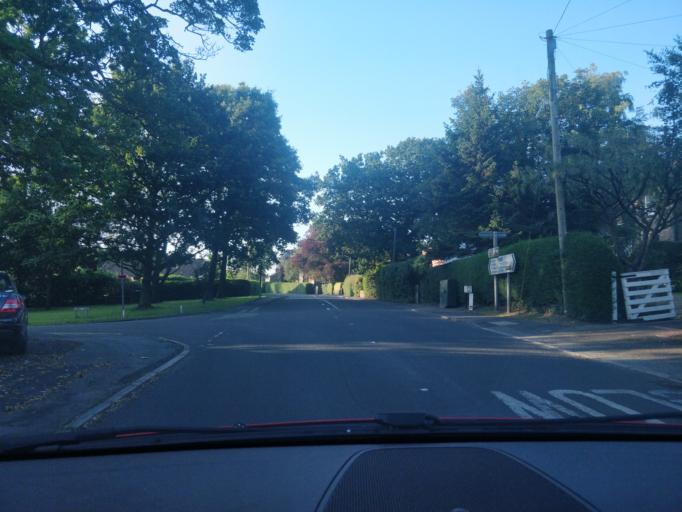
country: GB
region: England
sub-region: Lancashire
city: Parbold
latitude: 53.6020
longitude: -2.7655
